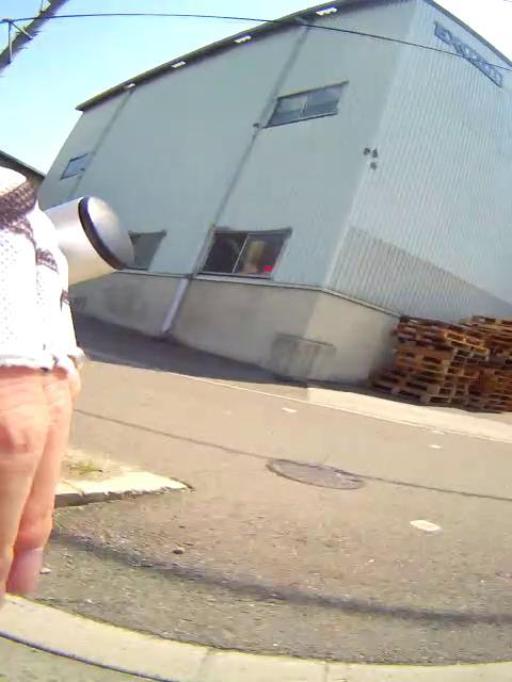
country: JP
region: Osaka
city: Matsubara
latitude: 34.5902
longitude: 135.5503
